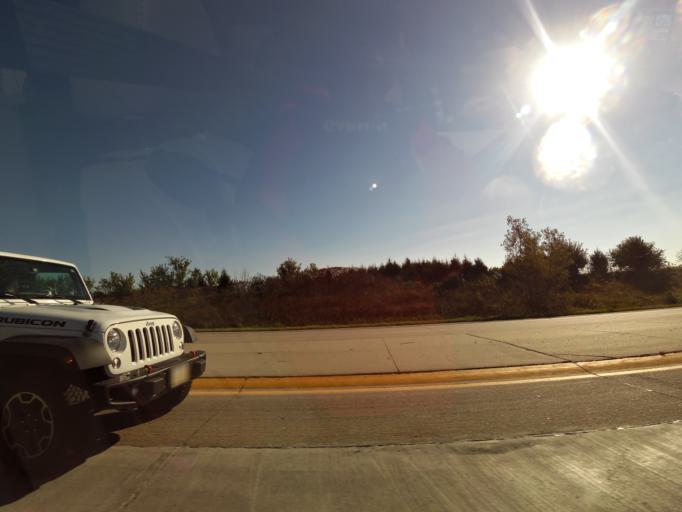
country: US
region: Nebraska
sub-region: Sarpy County
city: Gretna
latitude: 41.1085
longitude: -96.2534
